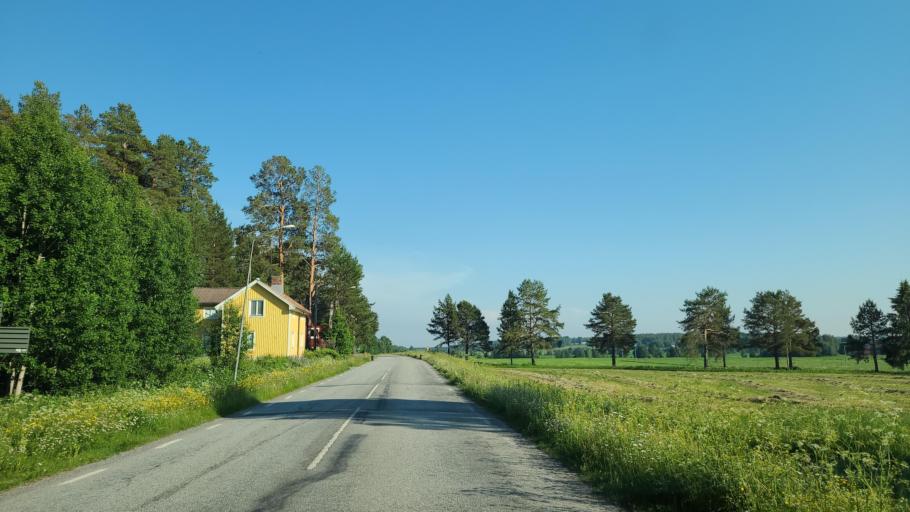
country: SE
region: Vaesterbotten
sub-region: Robertsfors Kommun
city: Robertsfors
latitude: 64.3003
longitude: 20.8783
